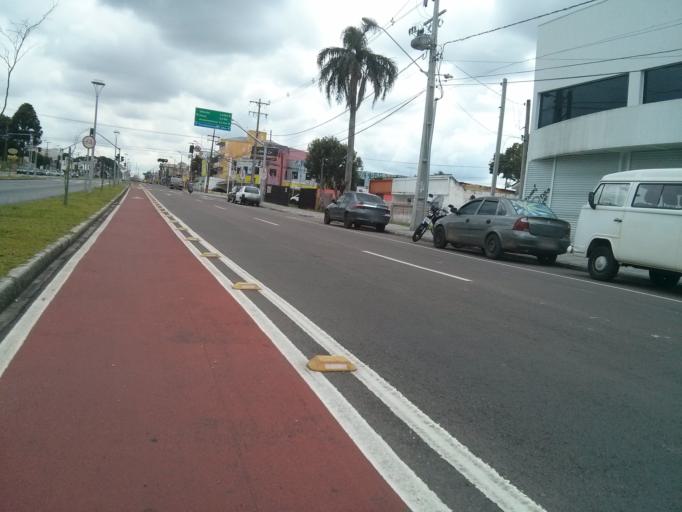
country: BR
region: Parana
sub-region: Sao Jose Dos Pinhais
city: Sao Jose dos Pinhais
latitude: -25.5148
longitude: -49.2310
